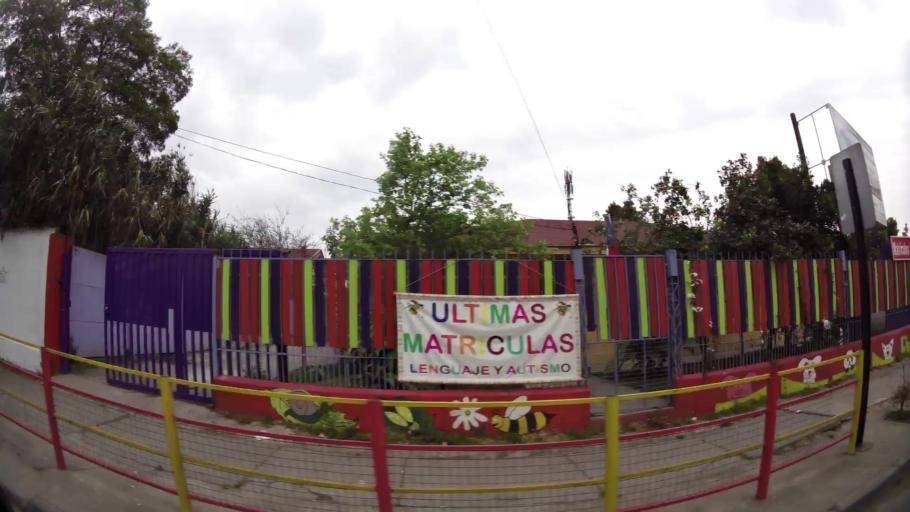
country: CL
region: Santiago Metropolitan
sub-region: Provincia de Santiago
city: Lo Prado
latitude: -33.4987
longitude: -70.7633
